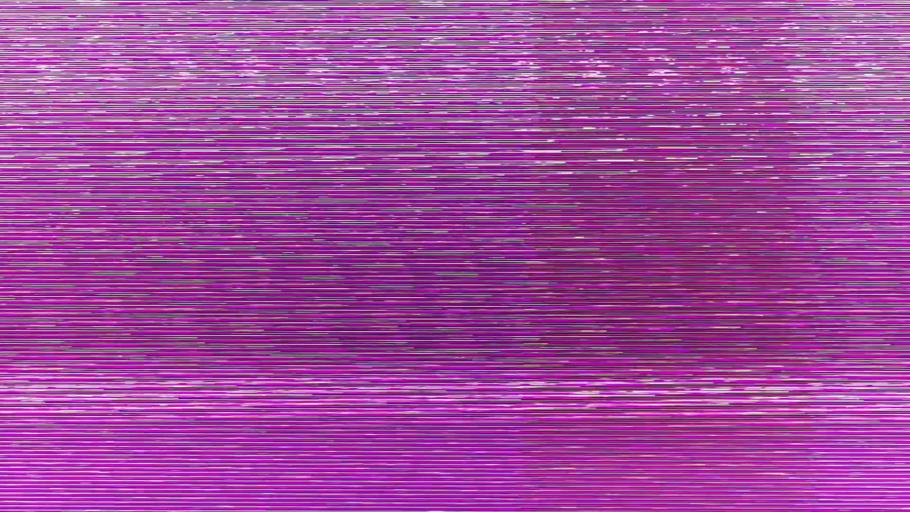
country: US
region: Michigan
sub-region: Livingston County
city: Whitmore Lake
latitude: 42.4420
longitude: -83.8266
